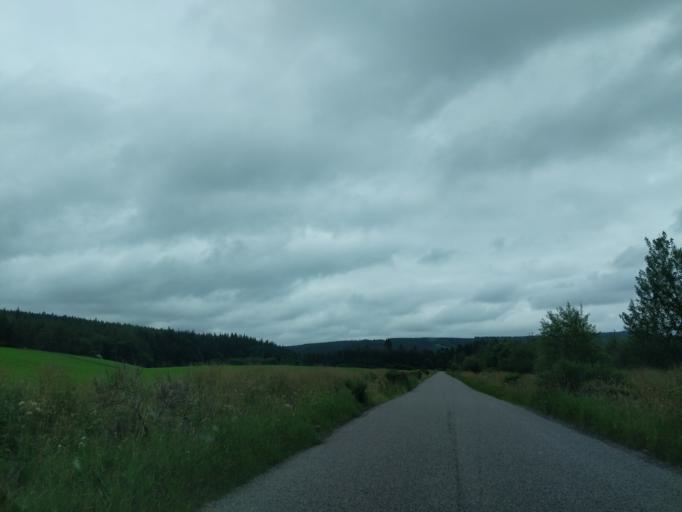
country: GB
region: Scotland
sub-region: Moray
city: Kinloss
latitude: 57.5510
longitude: -3.4965
